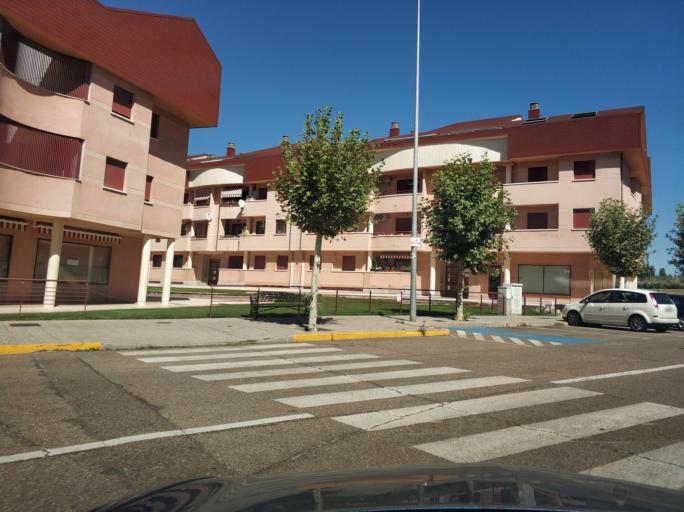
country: ES
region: Castille and Leon
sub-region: Provincia de Salamanca
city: Carbajosa de la Sagrada
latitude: 40.9500
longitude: -5.6483
